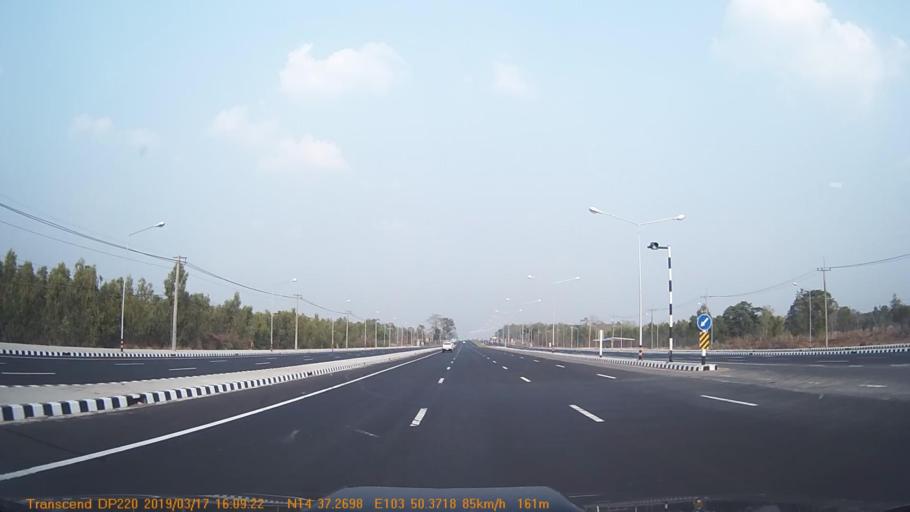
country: TH
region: Surin
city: Sangkha
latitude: 14.6214
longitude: 103.8400
